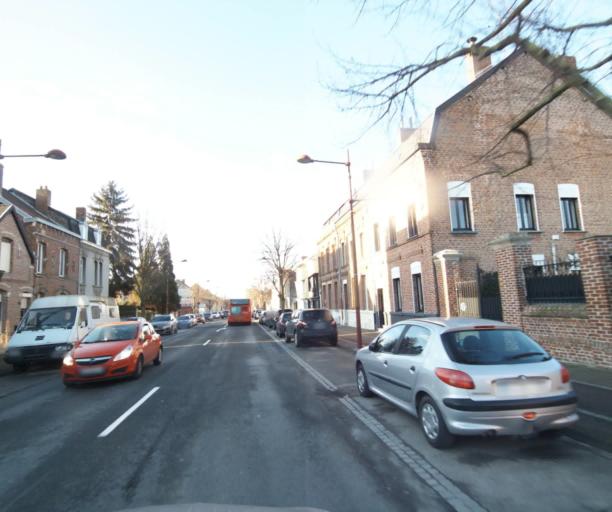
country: FR
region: Nord-Pas-de-Calais
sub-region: Departement du Nord
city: Marly
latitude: 50.3488
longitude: 3.5476
